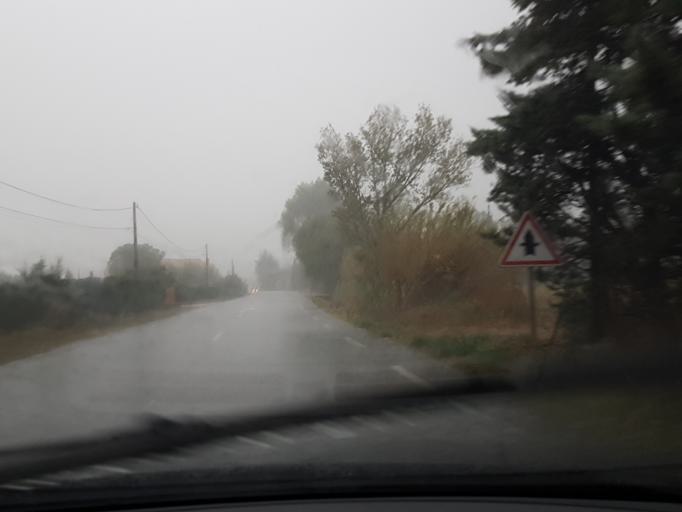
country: FR
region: Provence-Alpes-Cote d'Azur
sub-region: Departement du Vaucluse
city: Pernes-les-Fontaines
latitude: 44.0143
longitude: 5.0287
